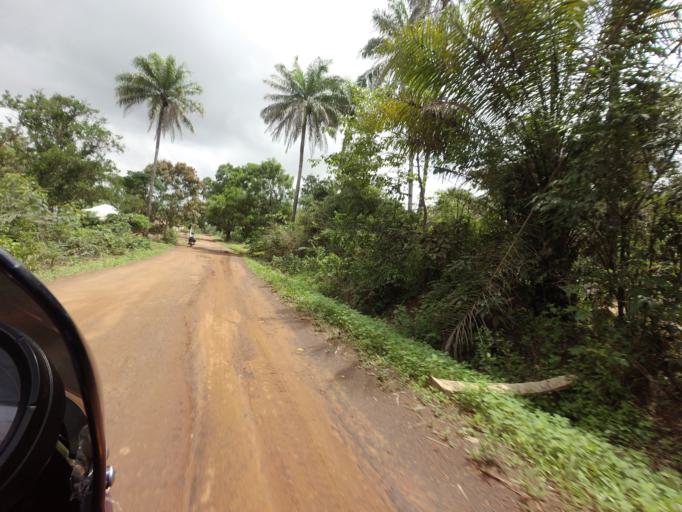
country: SL
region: Northern Province
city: Kambia
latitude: 9.1043
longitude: -12.9650
